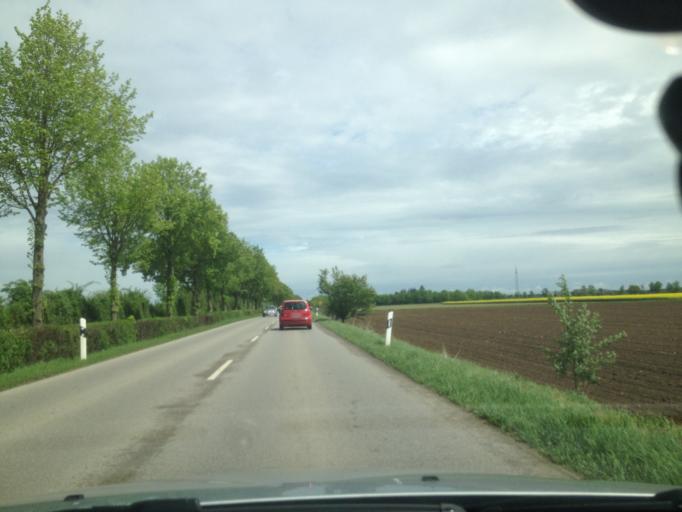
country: DE
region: Bavaria
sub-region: Swabia
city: Konigsbrunn
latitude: 48.3095
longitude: 10.8731
